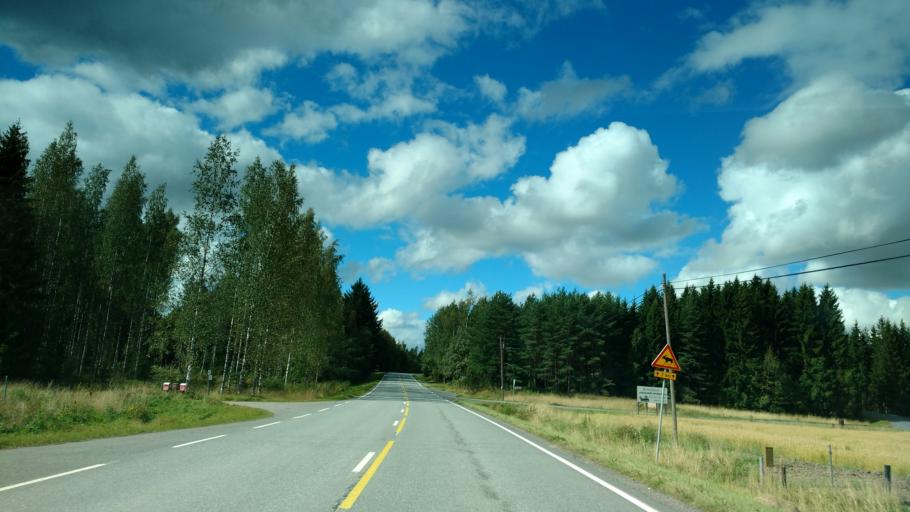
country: FI
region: Haeme
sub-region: Forssa
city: Ypaejae
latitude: 60.7974
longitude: 23.2639
